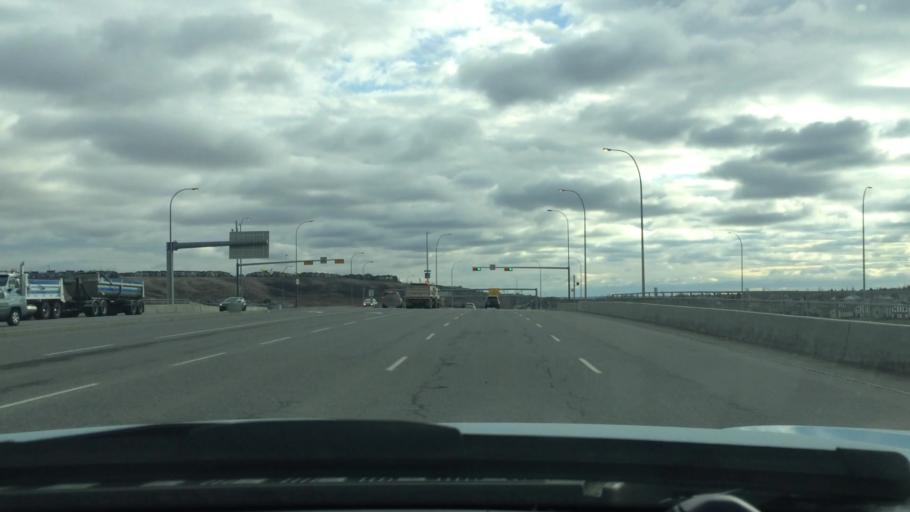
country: CA
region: Alberta
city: Calgary
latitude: 51.1568
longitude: -114.1166
